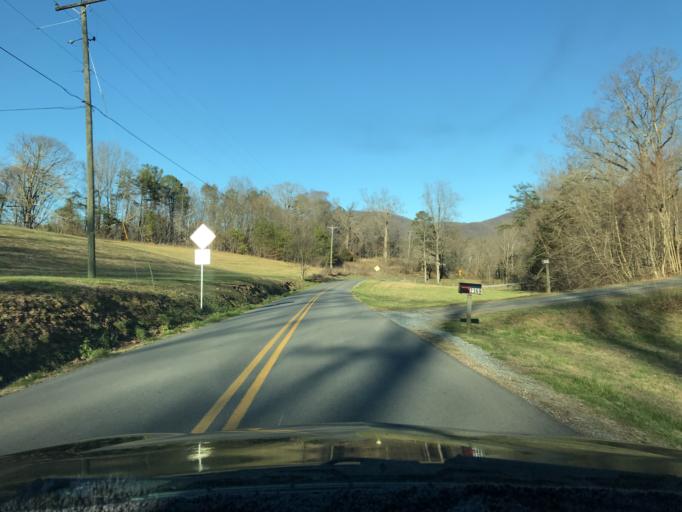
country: US
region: Virginia
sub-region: Botetourt County
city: Blue Ridge
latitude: 37.3937
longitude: -79.7140
